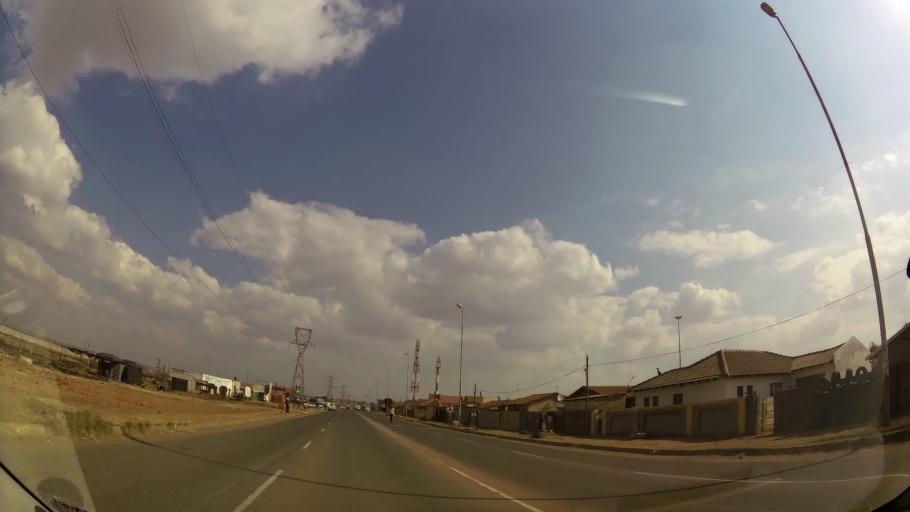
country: ZA
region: Gauteng
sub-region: Ekurhuleni Metropolitan Municipality
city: Springs
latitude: -26.1189
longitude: 28.4612
